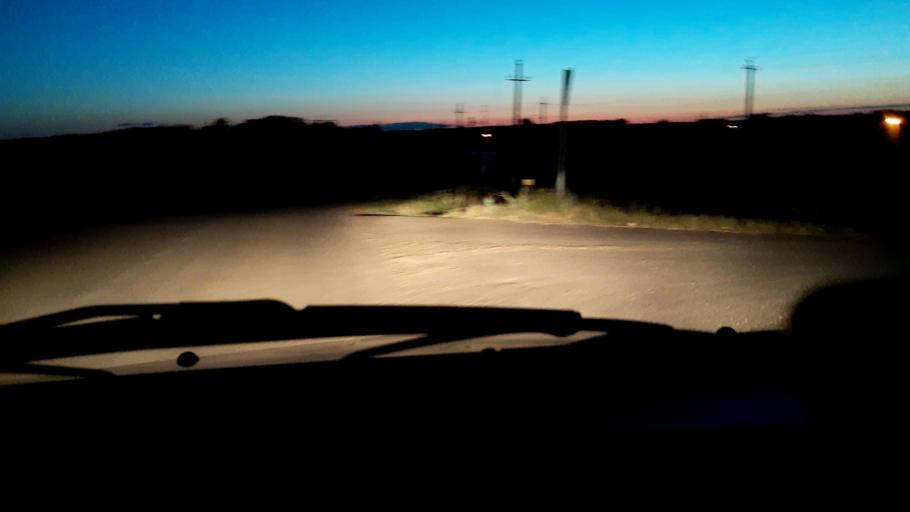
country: RU
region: Bashkortostan
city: Mikhaylovka
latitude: 54.9442
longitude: 55.8670
